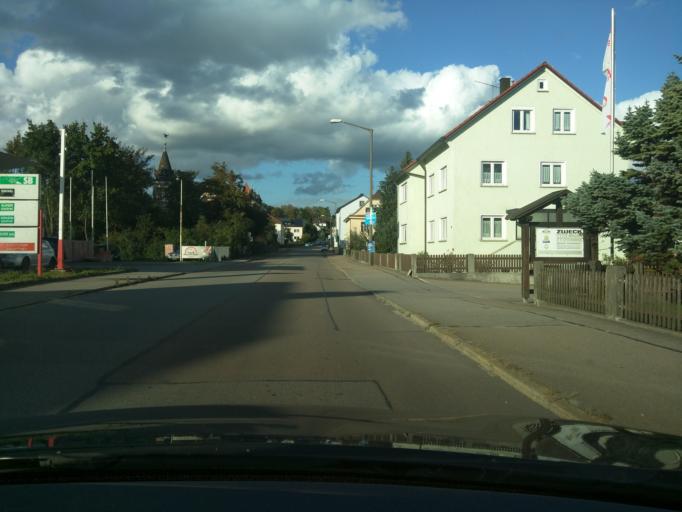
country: DE
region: Bavaria
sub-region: Upper Palatinate
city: Schwandorf in Bayern
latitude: 49.3401
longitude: 12.1232
